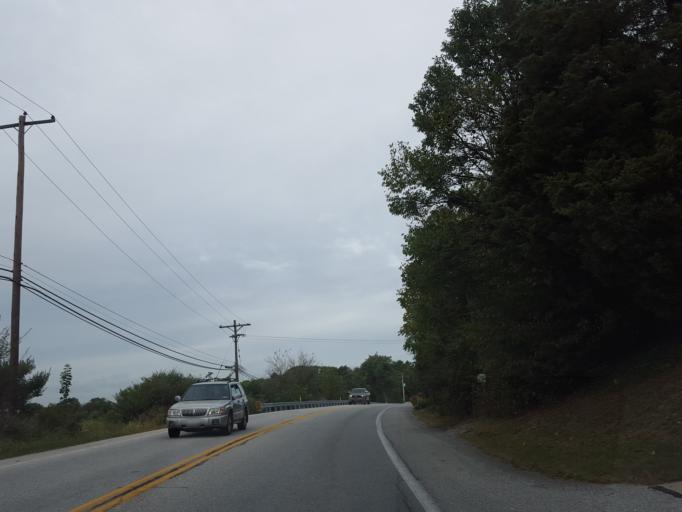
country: US
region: Pennsylvania
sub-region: York County
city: Shiloh
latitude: 39.9260
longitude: -76.8038
